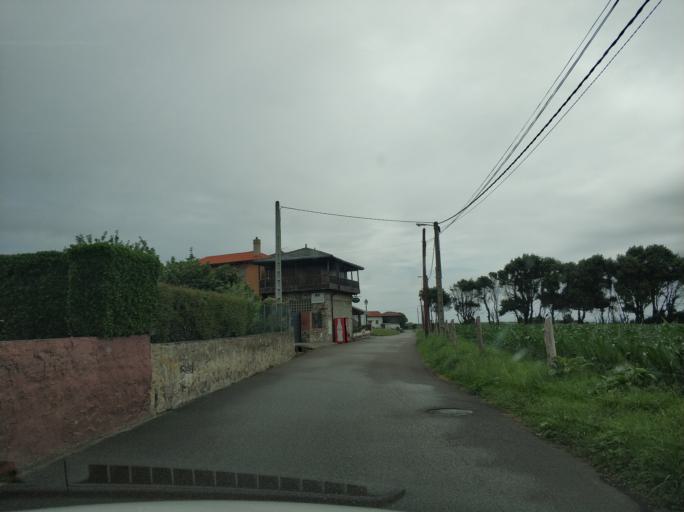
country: ES
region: Asturias
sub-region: Province of Asturias
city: Salas
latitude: 43.5521
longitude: -6.3792
